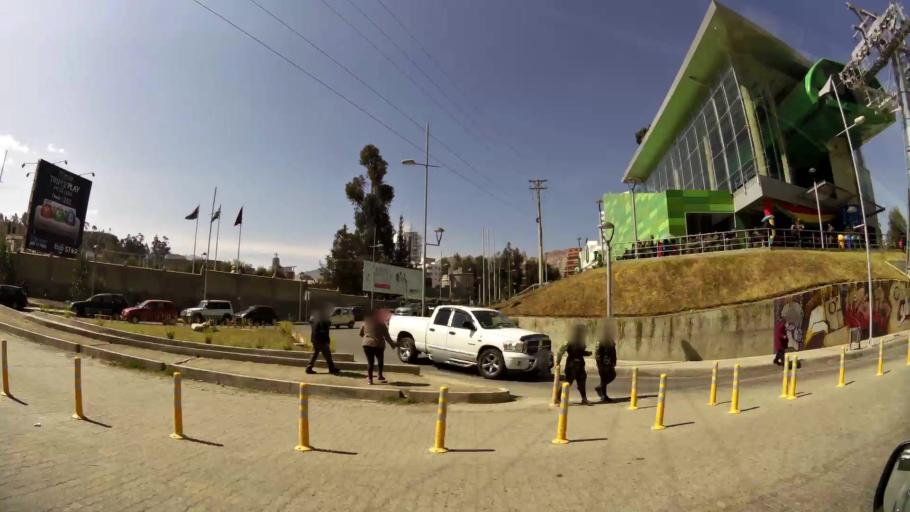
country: BO
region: La Paz
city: La Paz
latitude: -16.5378
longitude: -68.0875
